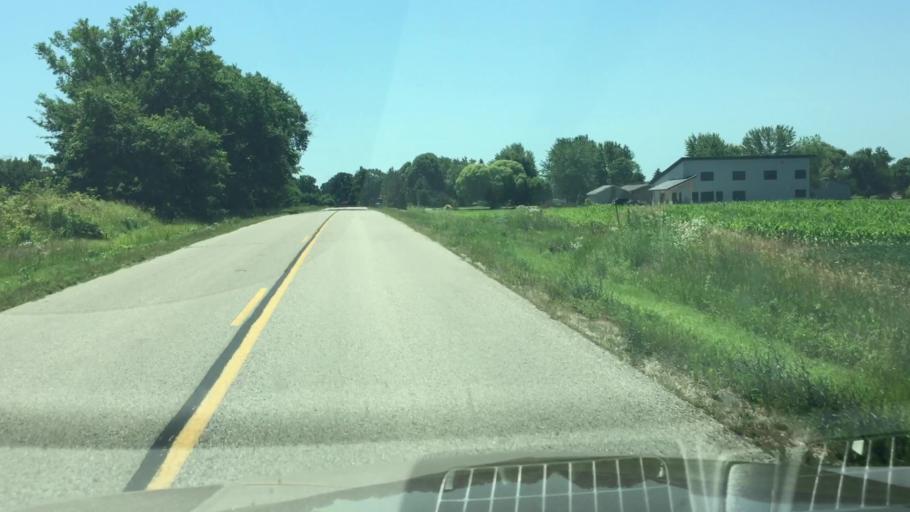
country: US
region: Wisconsin
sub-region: Fond du Lac County
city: Saint Peter
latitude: 43.9390
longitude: -88.3113
